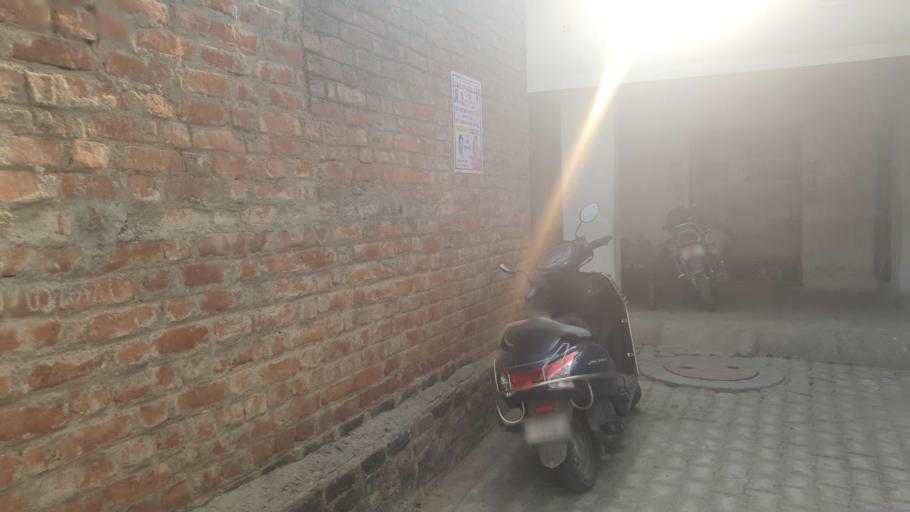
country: IN
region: Uttar Pradesh
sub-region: Lucknow District
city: Goshainganj
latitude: 26.7725
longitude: 81.0111
